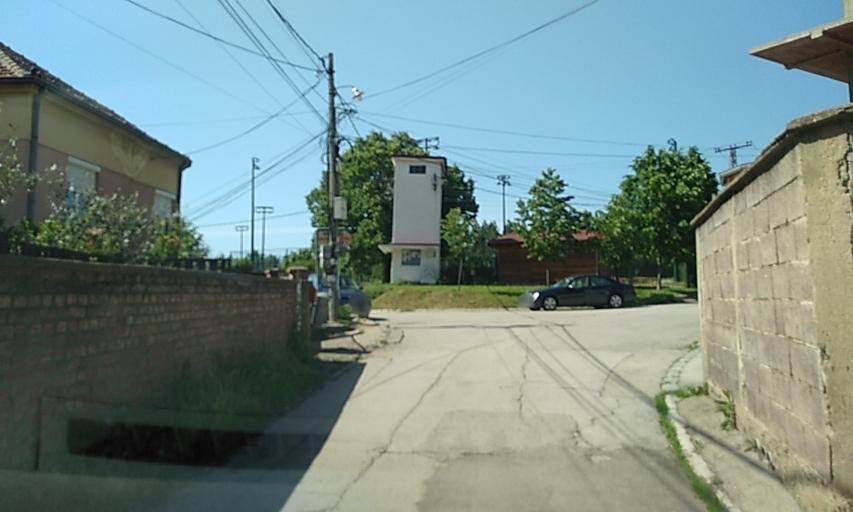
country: RS
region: Central Serbia
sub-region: Nisavski Okrug
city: Niska Banja
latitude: 43.2952
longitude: 22.0150
